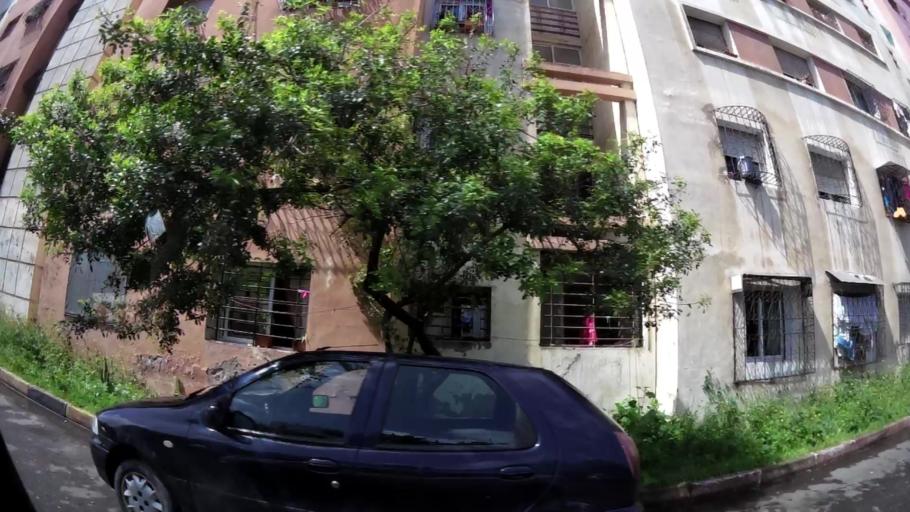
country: MA
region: Grand Casablanca
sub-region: Mediouna
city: Tit Mellil
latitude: 33.6142
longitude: -7.5262
